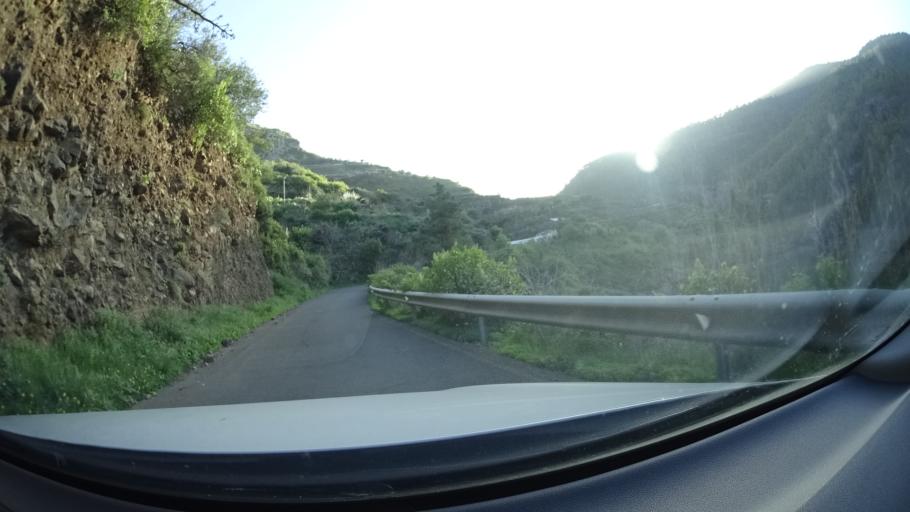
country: ES
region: Canary Islands
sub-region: Provincia de Las Palmas
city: Artenara
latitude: 28.0481
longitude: -15.6691
